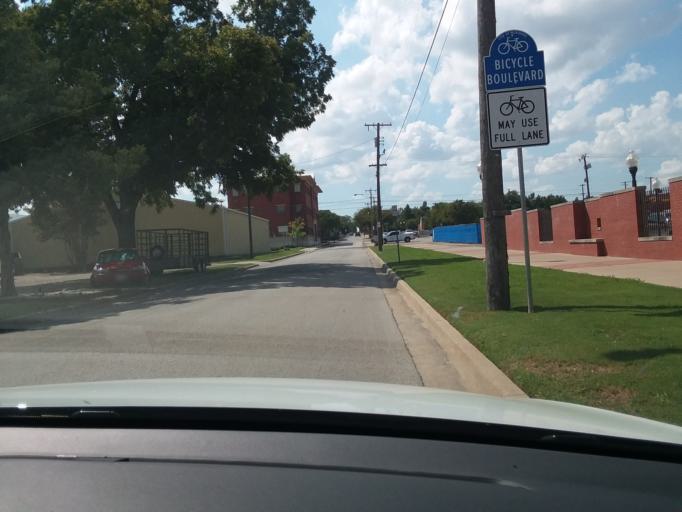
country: US
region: Texas
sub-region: Collin County
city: McKinney
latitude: 33.1994
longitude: -96.6126
